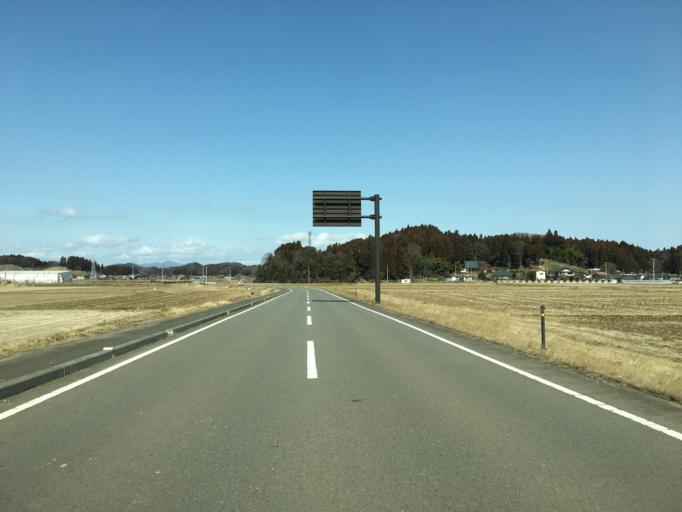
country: JP
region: Fukushima
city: Ishikawa
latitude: 37.1182
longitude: 140.2772
